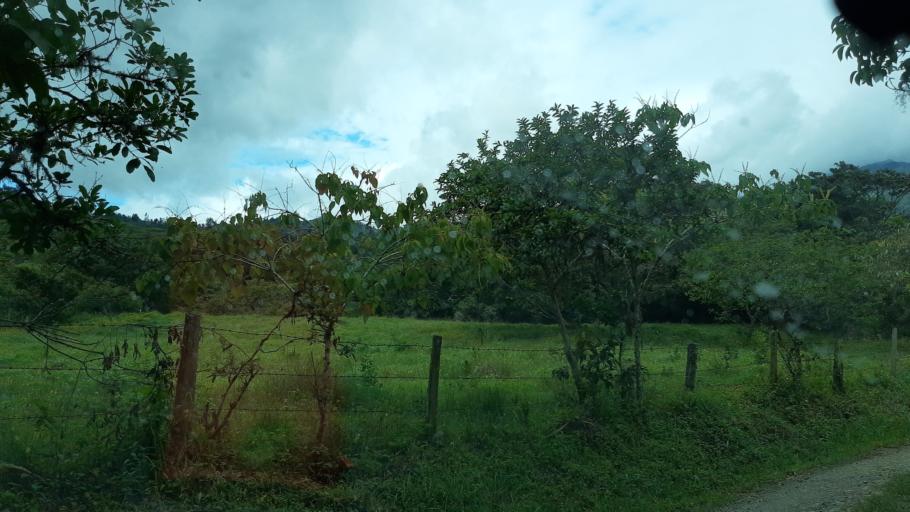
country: CO
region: Boyaca
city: Garagoa
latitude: 5.0374
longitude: -73.3566
